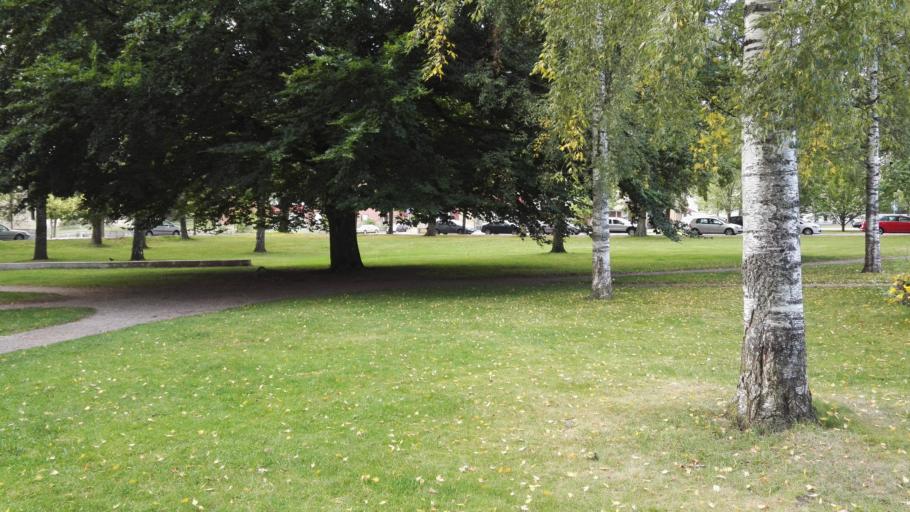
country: SE
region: Kronoberg
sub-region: Vaxjo Kommun
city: Vaexjoe
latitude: 56.8728
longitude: 14.8056
